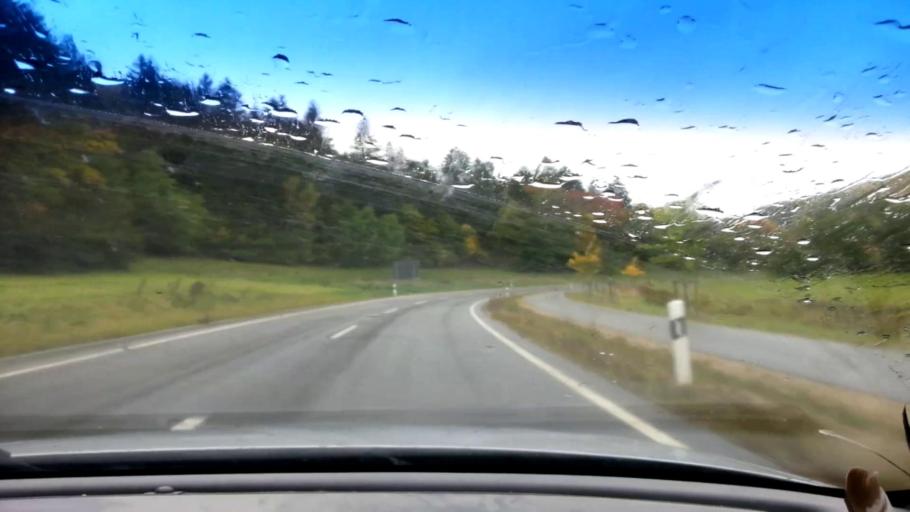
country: DE
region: Bavaria
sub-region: Upper Franconia
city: Heiligenstadt
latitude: 49.8689
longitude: 11.1656
